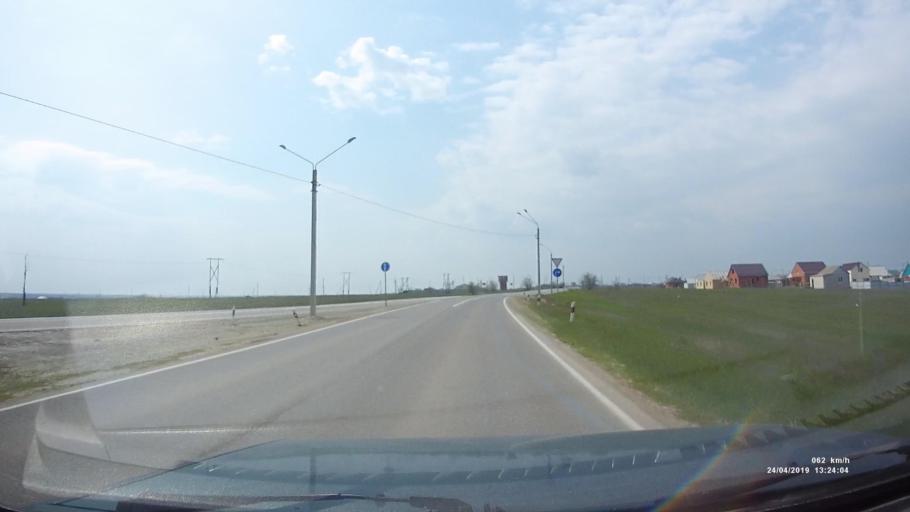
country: RU
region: Kalmykiya
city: Elista
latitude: 46.2834
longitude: 44.2602
